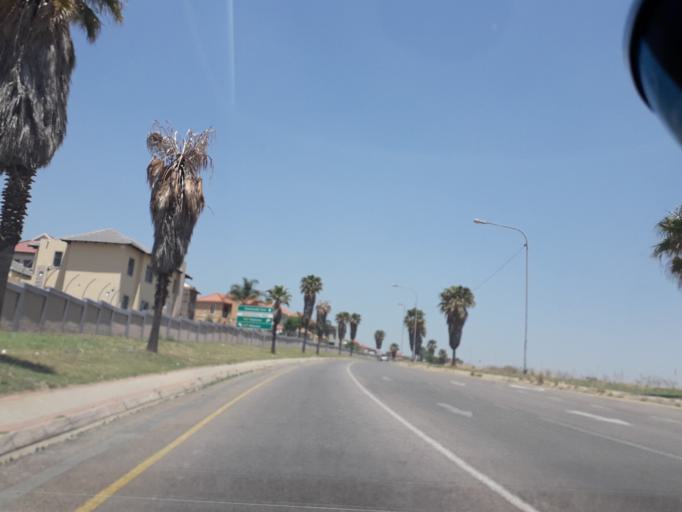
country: ZA
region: Gauteng
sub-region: City of Johannesburg Metropolitan Municipality
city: Midrand
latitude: -25.9309
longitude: 28.1352
